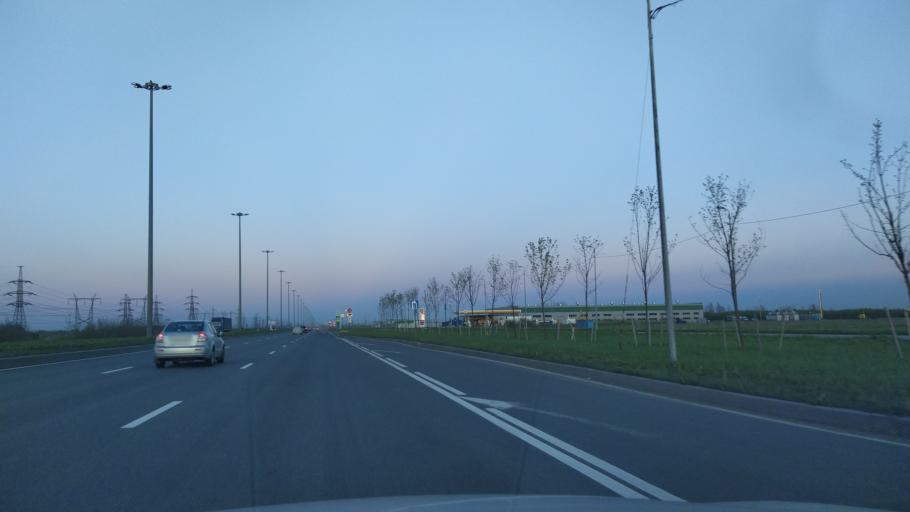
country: RU
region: St.-Petersburg
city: Obukhovo
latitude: 59.8086
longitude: 30.4670
